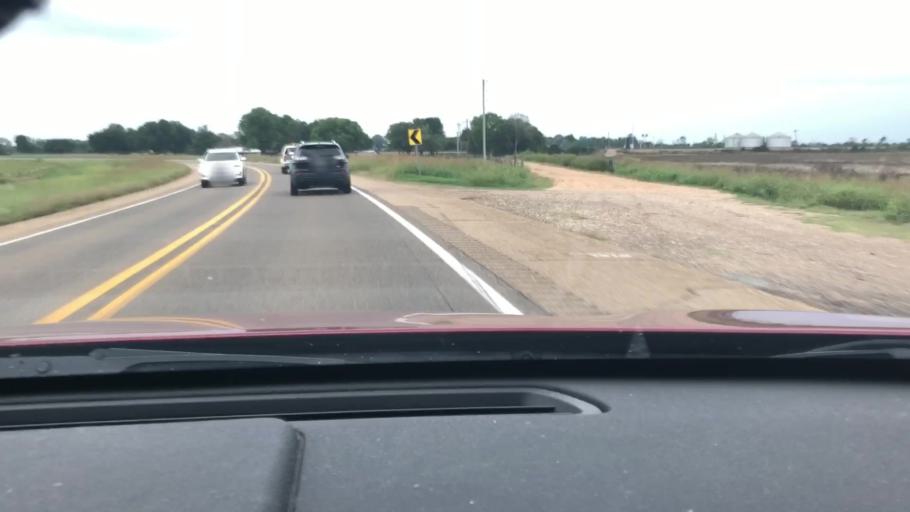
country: US
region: Arkansas
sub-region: Lafayette County
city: Lewisville
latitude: 33.3792
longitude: -93.7360
